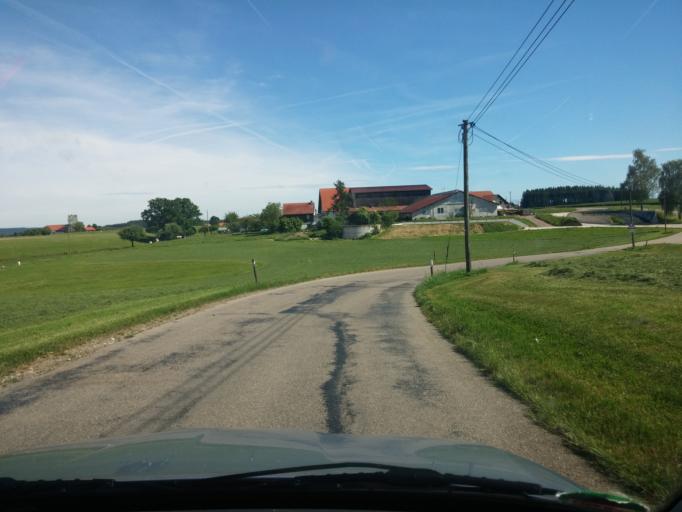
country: DE
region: Bavaria
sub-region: Swabia
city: Woringen
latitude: 47.8944
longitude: 10.1848
